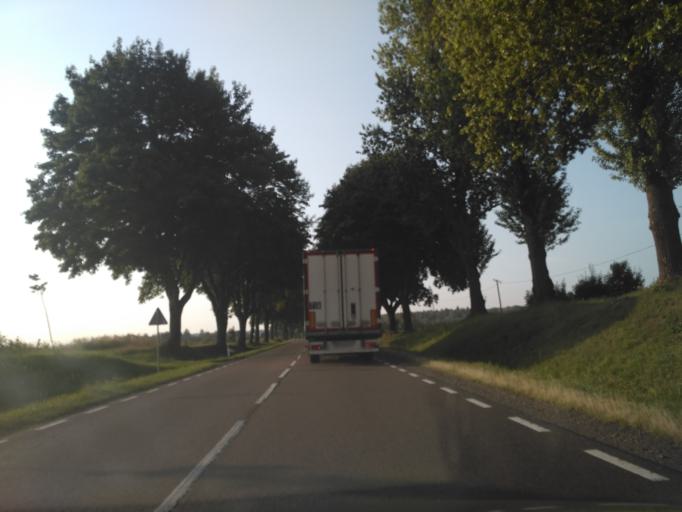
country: PL
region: Lublin Voivodeship
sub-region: Powiat krasnicki
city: Krasnik
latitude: 50.8795
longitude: 22.2632
